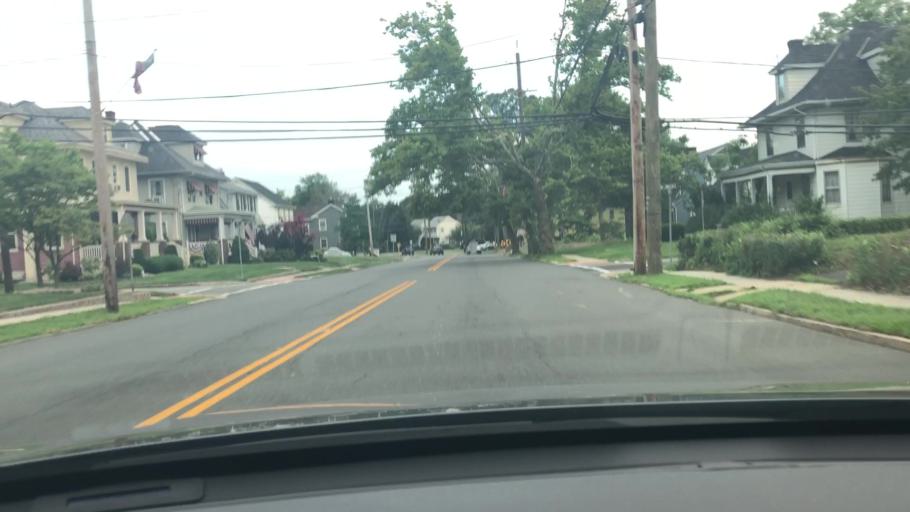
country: US
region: New Jersey
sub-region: Middlesex County
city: Milltown
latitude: 40.4609
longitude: -74.4462
